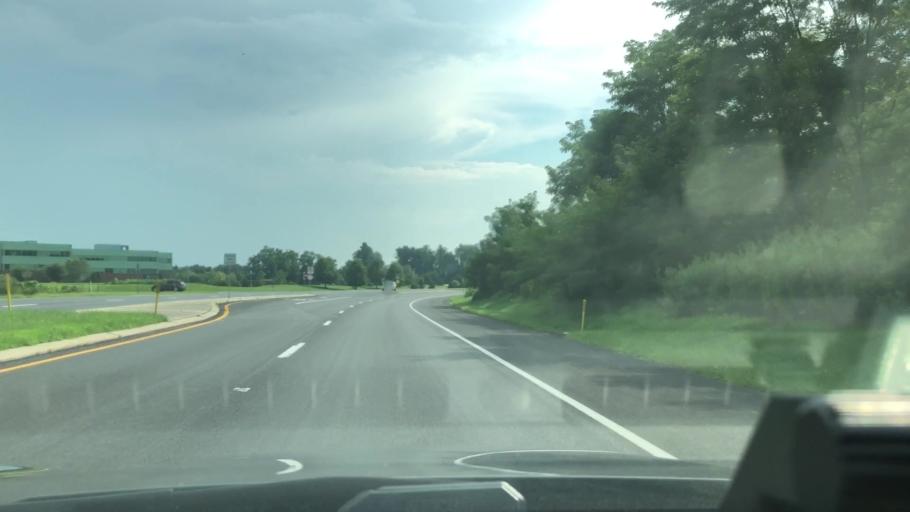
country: US
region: Pennsylvania
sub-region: Lehigh County
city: Fountain Hill
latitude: 40.5617
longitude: -75.4021
